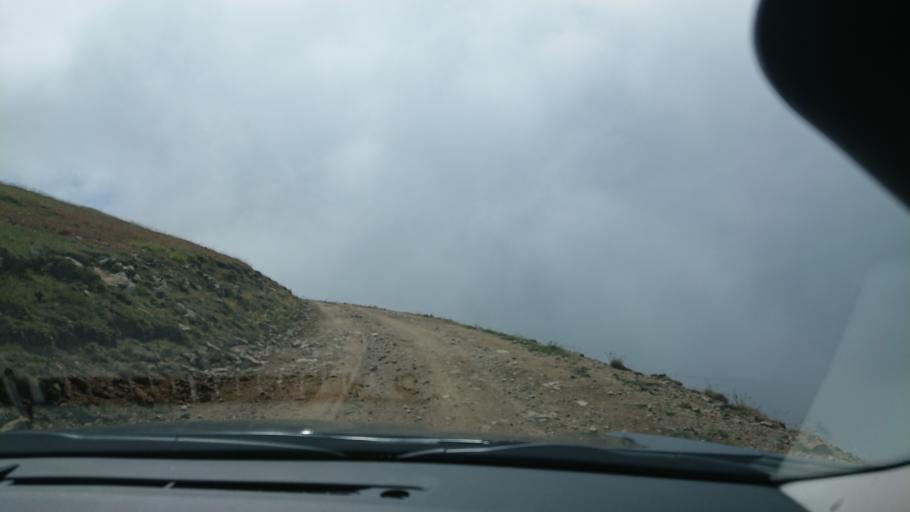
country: TR
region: Gumushane
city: Kurtun
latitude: 40.6273
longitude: 38.9947
